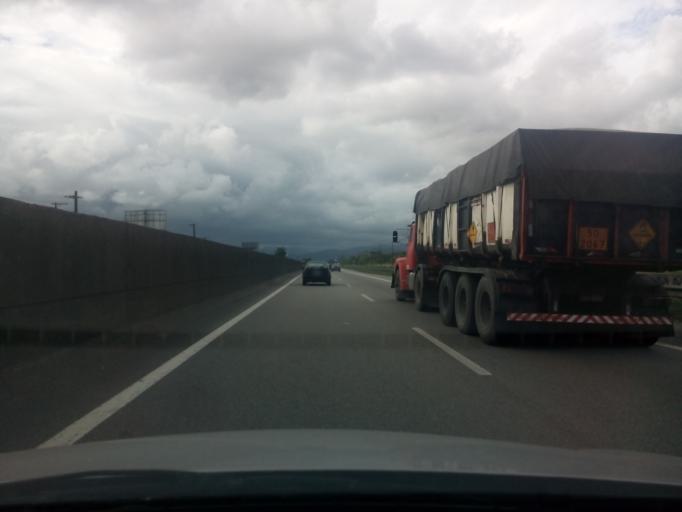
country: BR
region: Sao Paulo
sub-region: Guaruja
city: Guaruja
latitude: -23.9652
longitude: -46.2718
